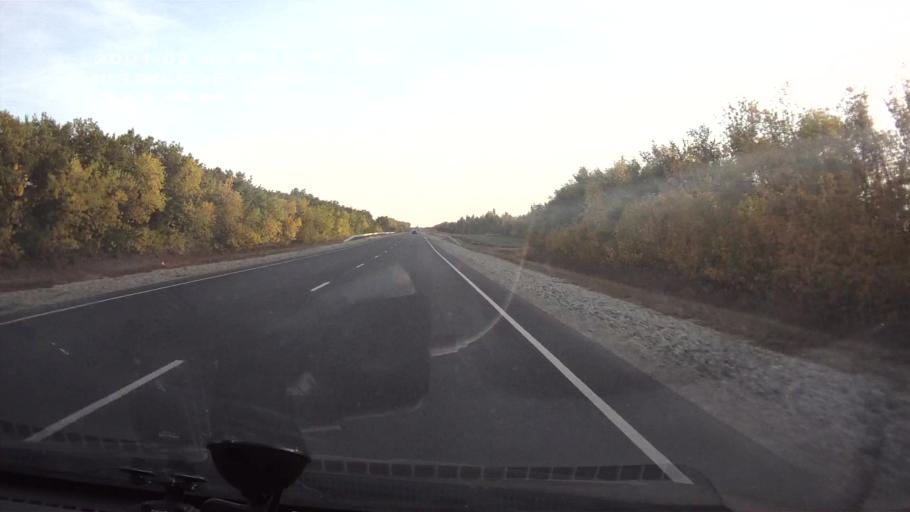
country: RU
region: Saratov
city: Krasnoarmeysk
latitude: 51.0850
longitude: 45.6444
